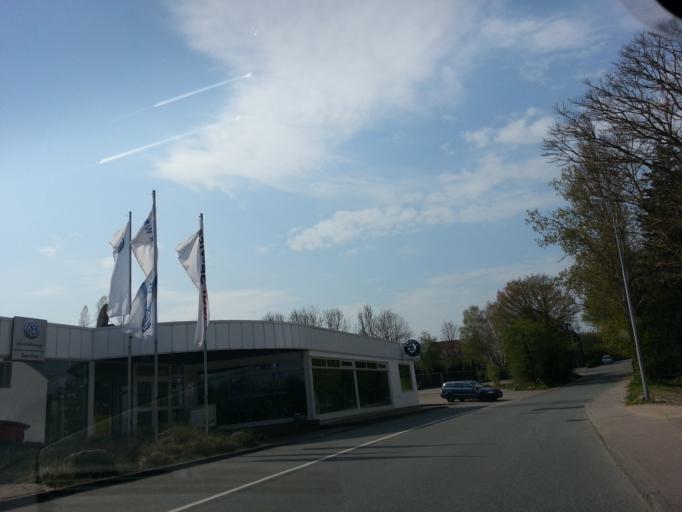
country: DE
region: Schleswig-Holstein
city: Timmendorfer Strand
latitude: 53.9879
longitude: 10.7704
